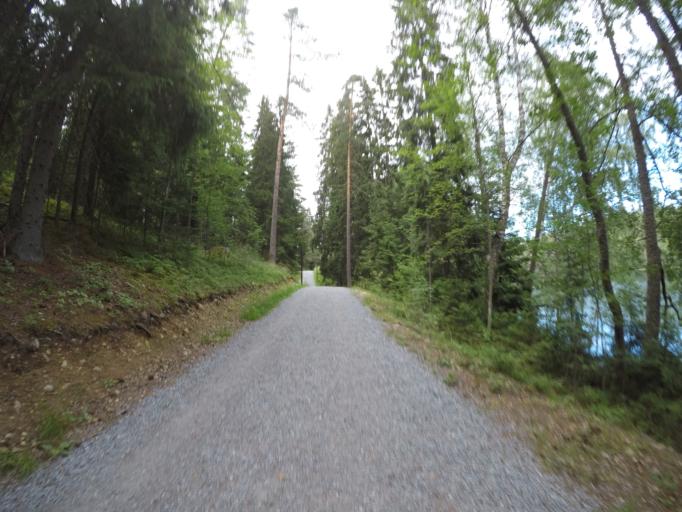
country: FI
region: Haeme
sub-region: Haemeenlinna
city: Haemeenlinna
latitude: 60.9949
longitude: 24.4147
